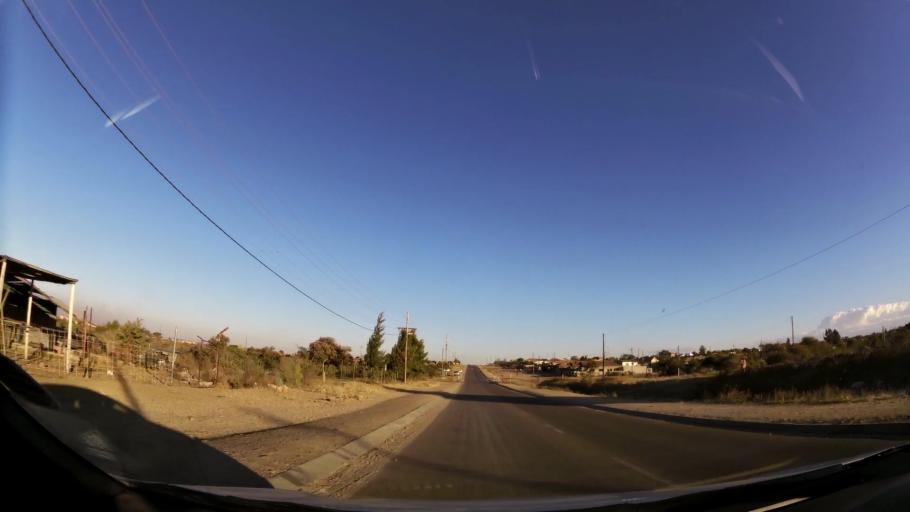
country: ZA
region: Limpopo
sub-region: Capricorn District Municipality
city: Polokwane
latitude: -23.8420
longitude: 29.3526
